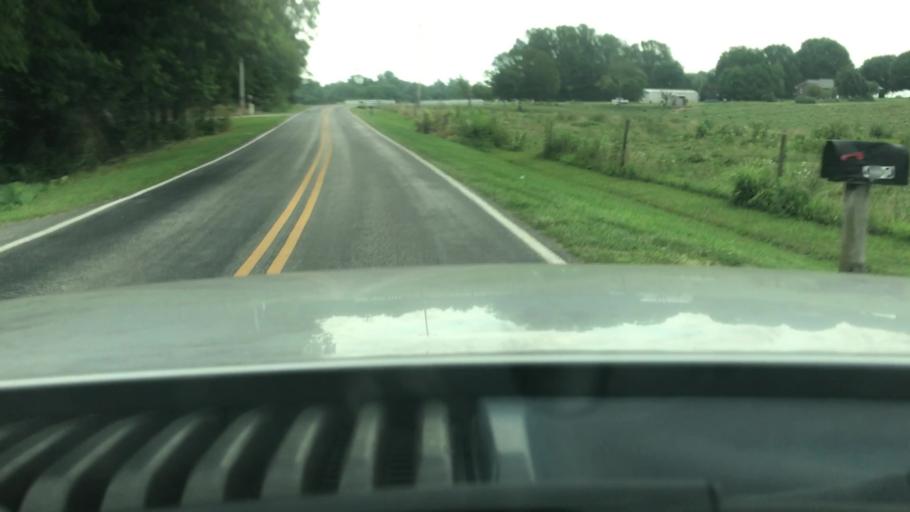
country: US
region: North Carolina
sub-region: Surry County
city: Dobson
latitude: 36.4041
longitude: -80.8074
